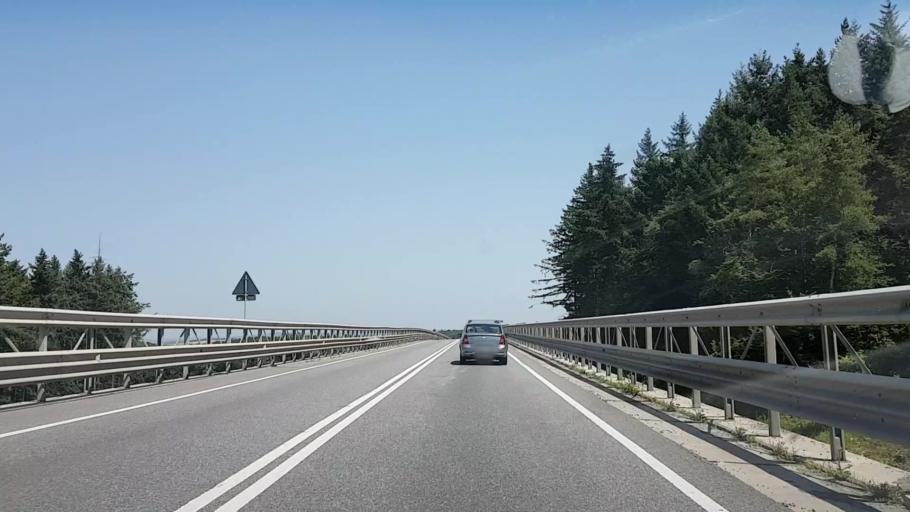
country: RO
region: Cluj
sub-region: Comuna Feleacu
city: Feleacu
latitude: 46.7283
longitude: 23.6515
